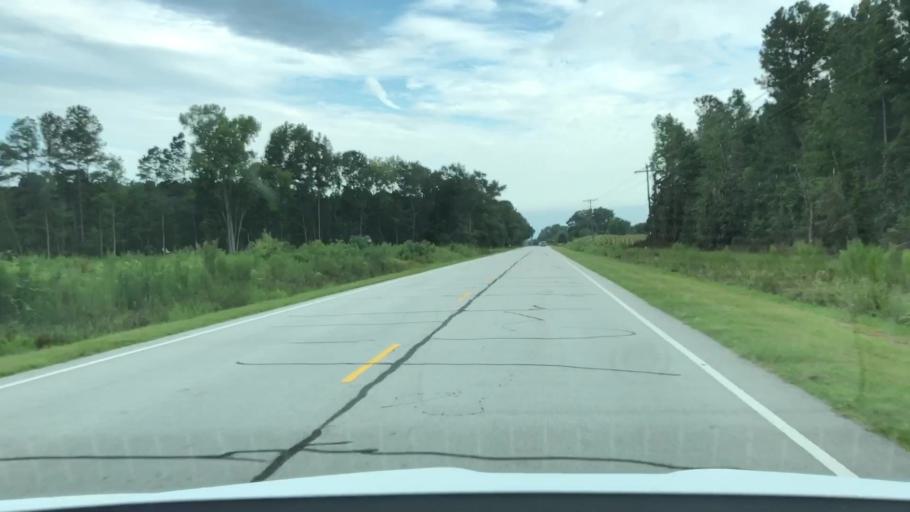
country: US
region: North Carolina
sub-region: Lenoir County
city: Kinston
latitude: 35.1307
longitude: -77.5241
